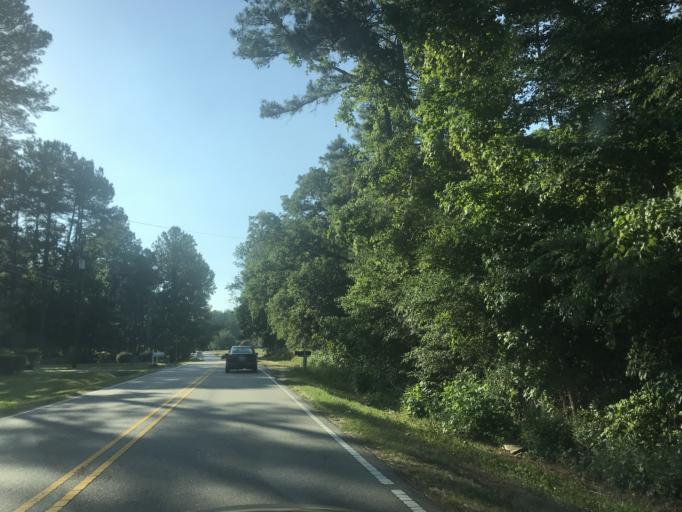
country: US
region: North Carolina
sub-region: Wake County
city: Garner
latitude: 35.7332
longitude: -78.6026
